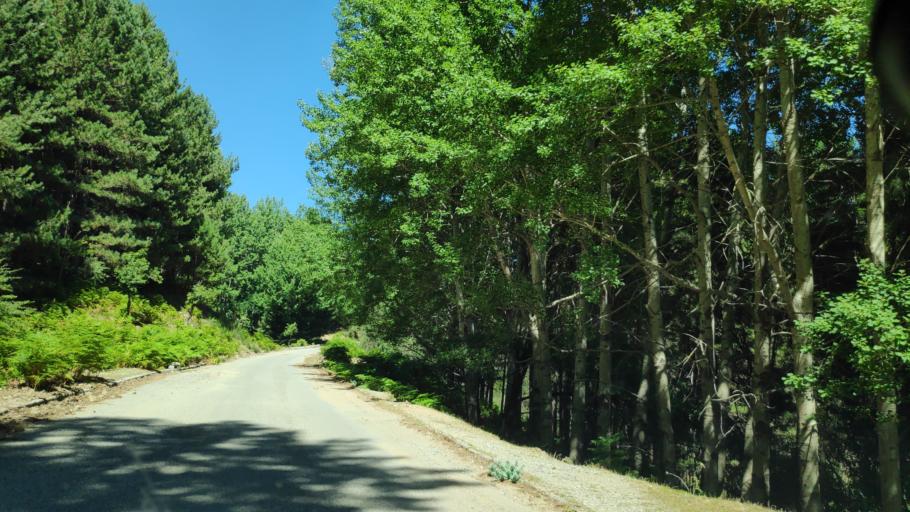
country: IT
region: Calabria
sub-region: Provincia di Reggio Calabria
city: Bova
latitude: 38.0341
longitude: 15.9486
